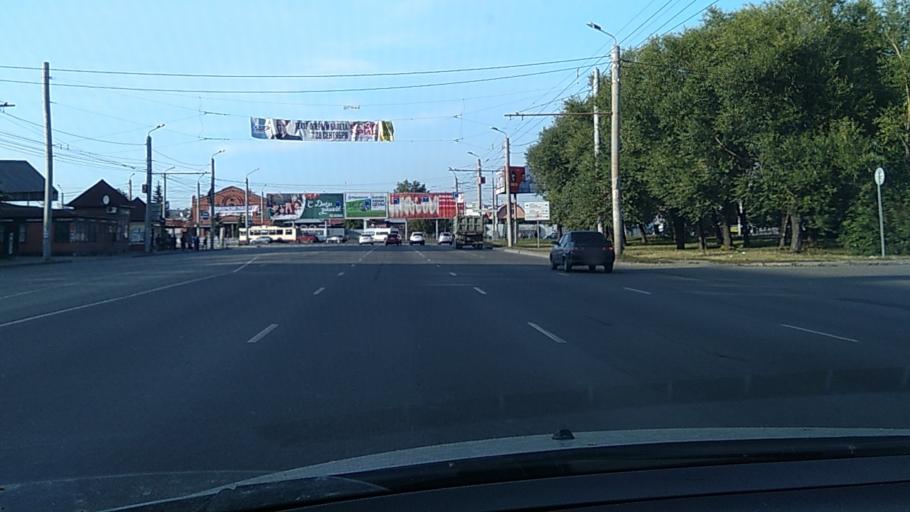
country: RU
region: Chelyabinsk
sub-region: Gorod Chelyabinsk
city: Chelyabinsk
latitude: 55.1773
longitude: 61.3583
